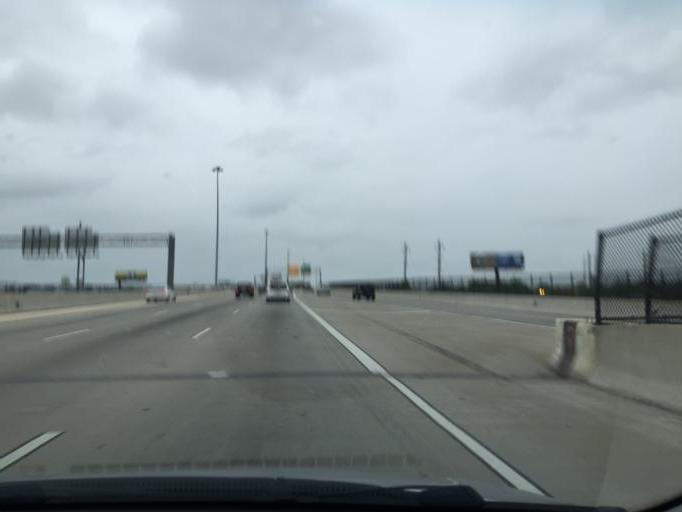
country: US
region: Maryland
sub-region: Baltimore County
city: Rosedale
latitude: 39.3007
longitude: -76.5307
